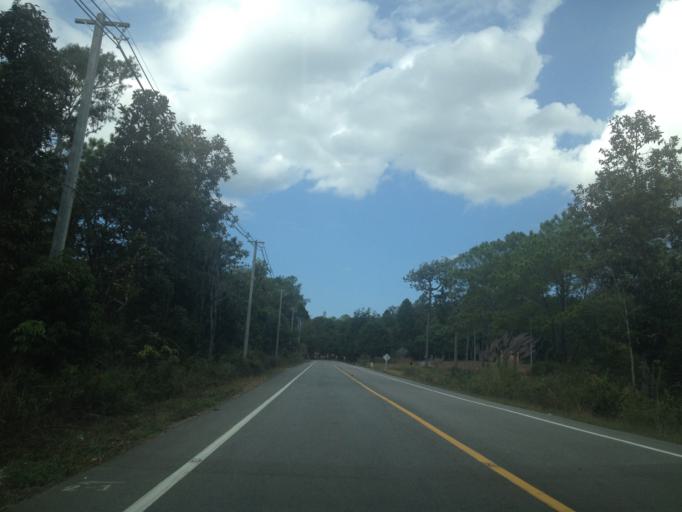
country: TH
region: Mae Hong Son
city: Pa Pae
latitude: 18.1587
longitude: 98.2858
